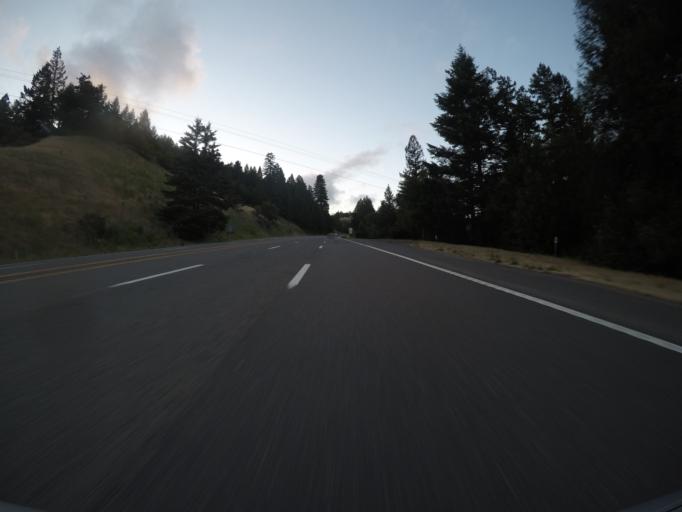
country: US
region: California
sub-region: Humboldt County
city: Redway
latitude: 40.0695
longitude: -123.7896
